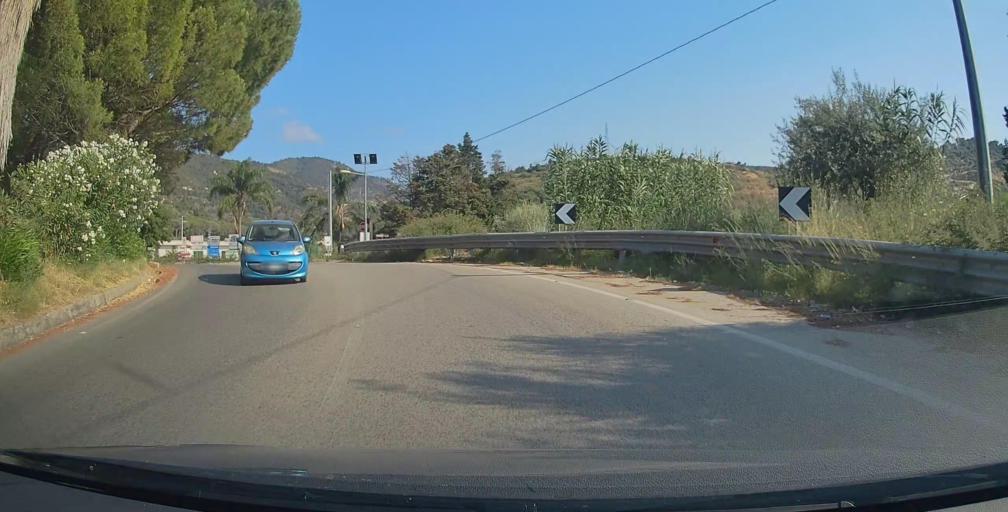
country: IT
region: Sicily
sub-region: Messina
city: Patti
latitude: 38.1375
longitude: 14.9969
